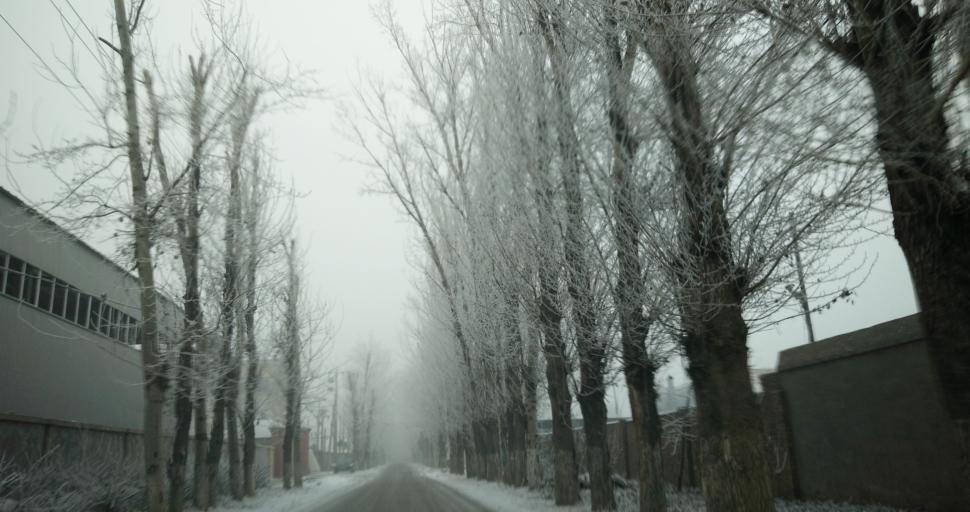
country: CN
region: Beijing
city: Yinghai
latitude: 39.7109
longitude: 116.4283
